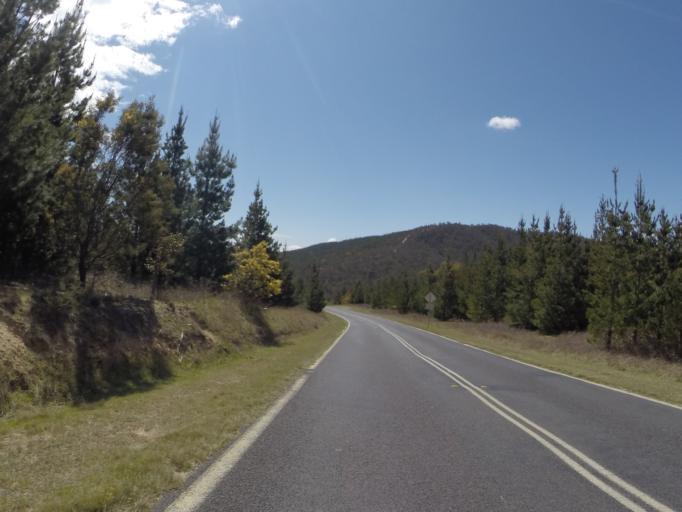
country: AU
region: Australian Capital Territory
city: Macquarie
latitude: -35.3730
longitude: 148.9611
